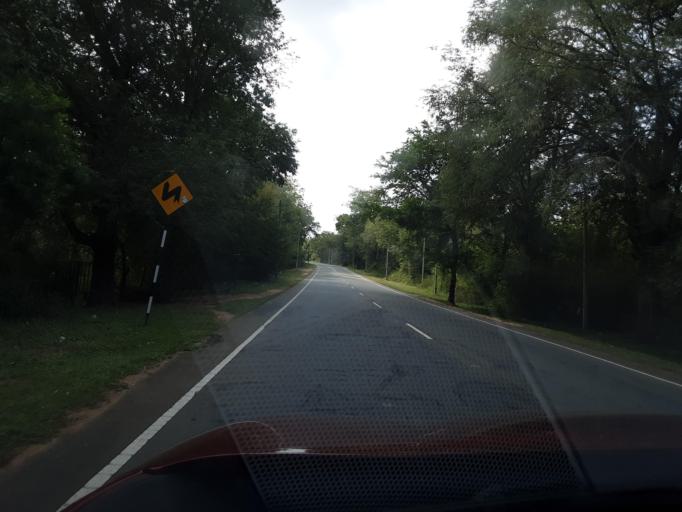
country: LK
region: Uva
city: Haputale
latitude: 6.3689
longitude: 81.1735
